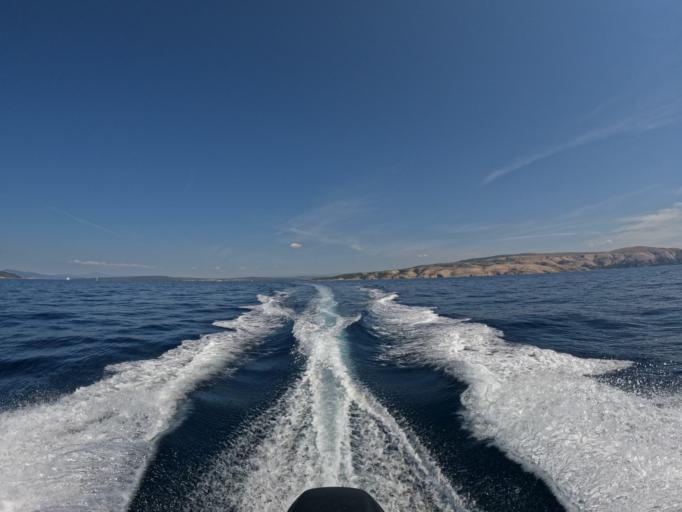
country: HR
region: Primorsko-Goranska
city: Punat
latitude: 44.9347
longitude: 14.6164
